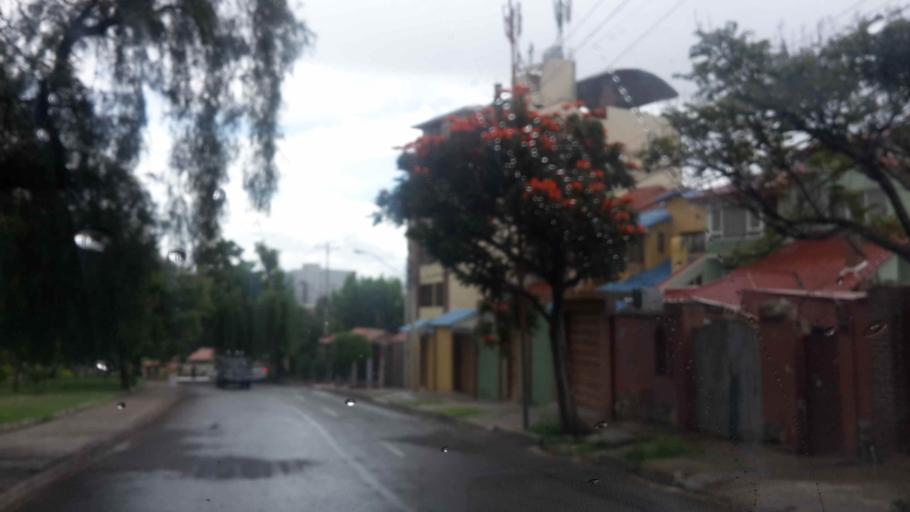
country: BO
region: Cochabamba
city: Cochabamba
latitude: -17.3672
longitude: -66.1578
